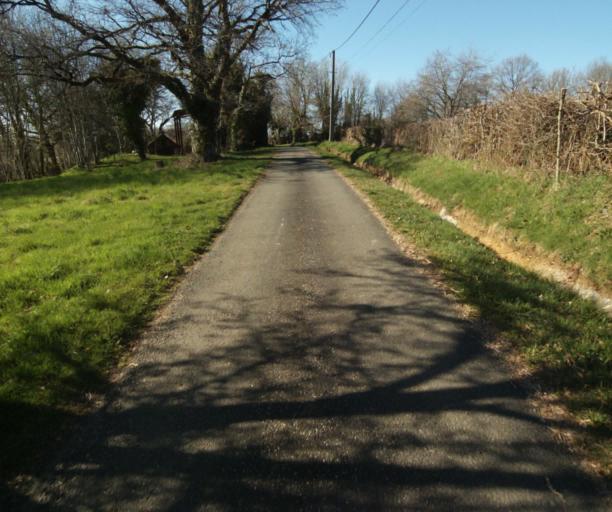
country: FR
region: Limousin
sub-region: Departement de la Correze
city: Chamboulive
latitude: 45.4050
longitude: 1.6609
